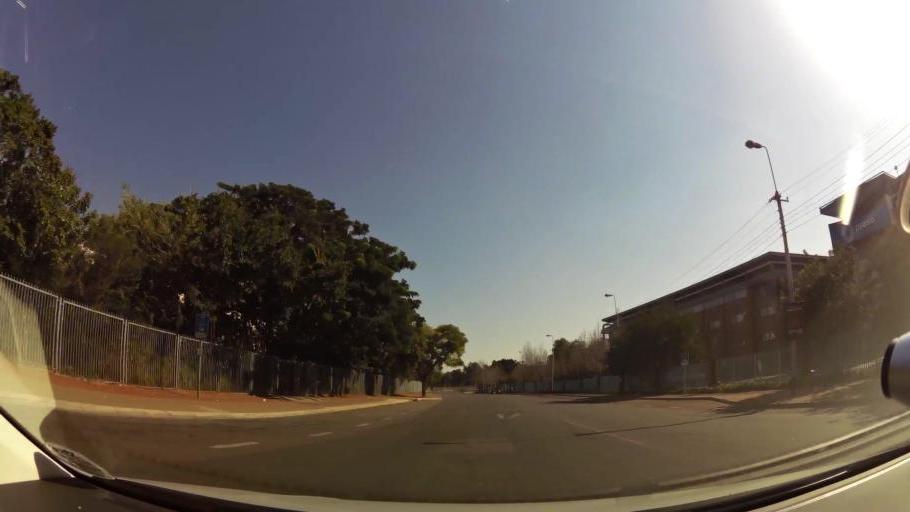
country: ZA
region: Gauteng
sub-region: City of Tshwane Metropolitan Municipality
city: Pretoria
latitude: -25.7509
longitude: 28.2315
